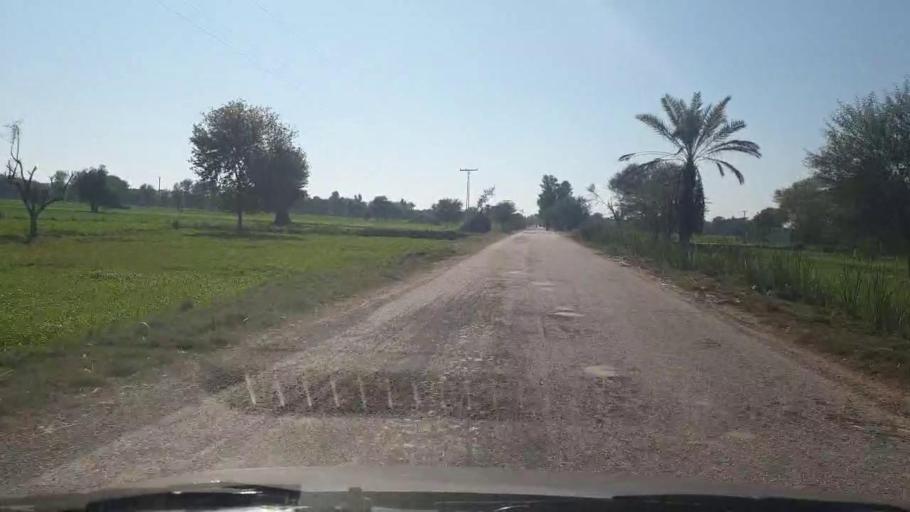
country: PK
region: Sindh
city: Bozdar
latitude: 27.1116
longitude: 68.6341
